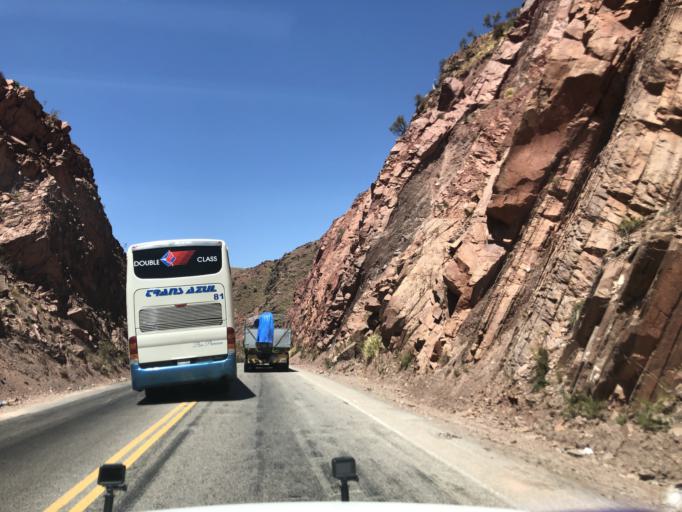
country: BO
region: Cochabamba
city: Irpa Irpa
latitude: -17.7202
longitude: -66.6187
